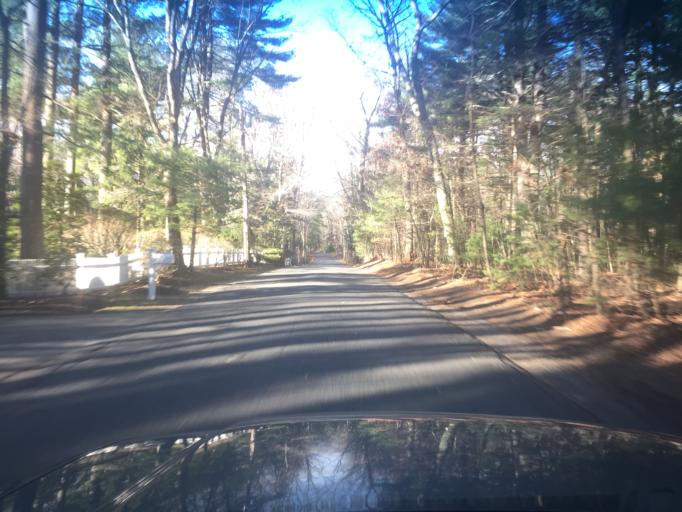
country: US
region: Massachusetts
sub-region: Middlesex County
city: Holliston
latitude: 42.2147
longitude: -71.4638
